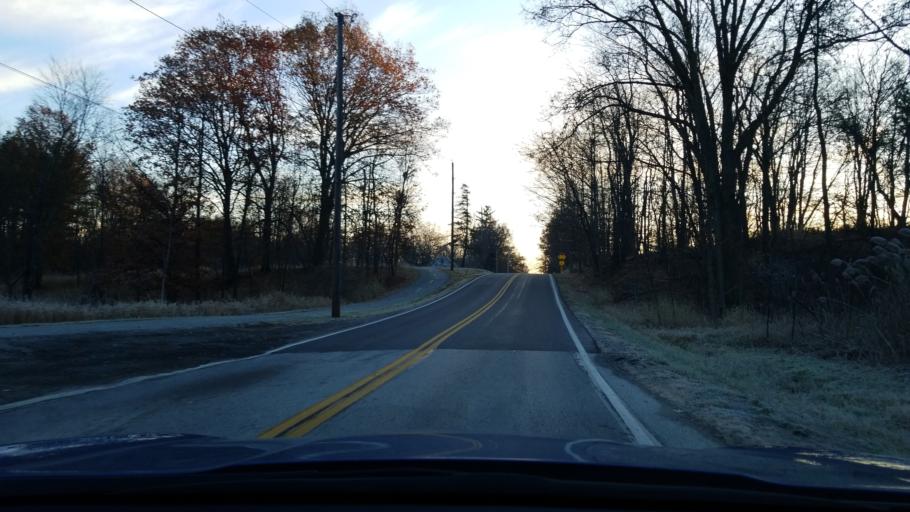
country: US
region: Ohio
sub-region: Cuyahoga County
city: Berea
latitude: 41.3428
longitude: -81.8427
